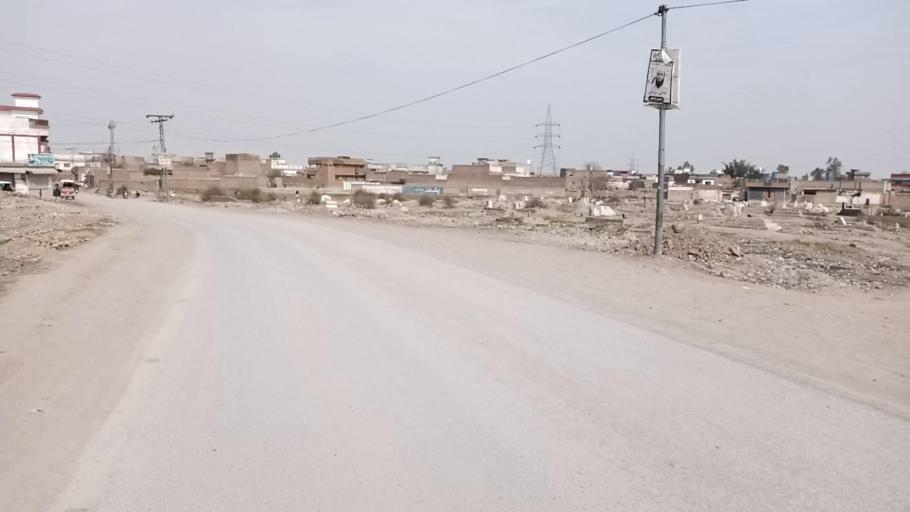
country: PK
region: Khyber Pakhtunkhwa
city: Peshawar
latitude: 33.9856
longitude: 71.4681
